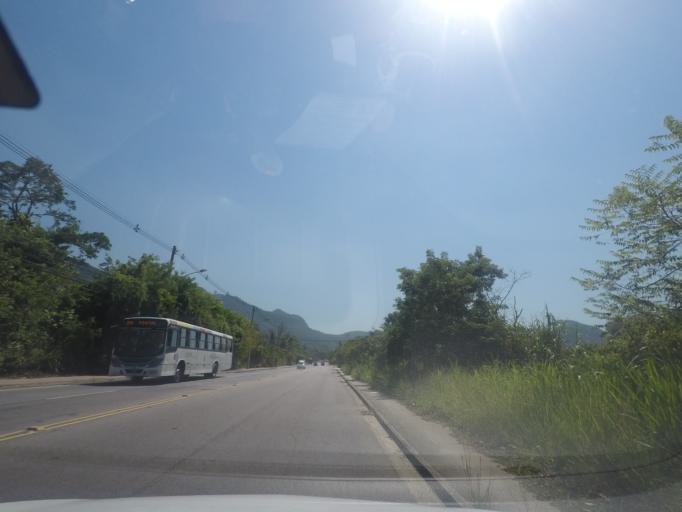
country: BR
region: Rio de Janeiro
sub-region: Nilopolis
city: Nilopolis
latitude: -22.9852
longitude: -43.4738
